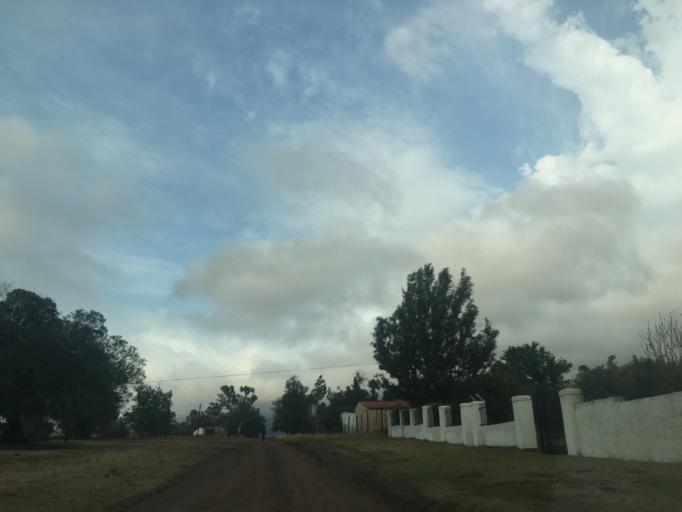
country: ZA
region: Eastern Cape
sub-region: Chris Hani District Municipality
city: Cala
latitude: -31.5234
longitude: 27.7019
